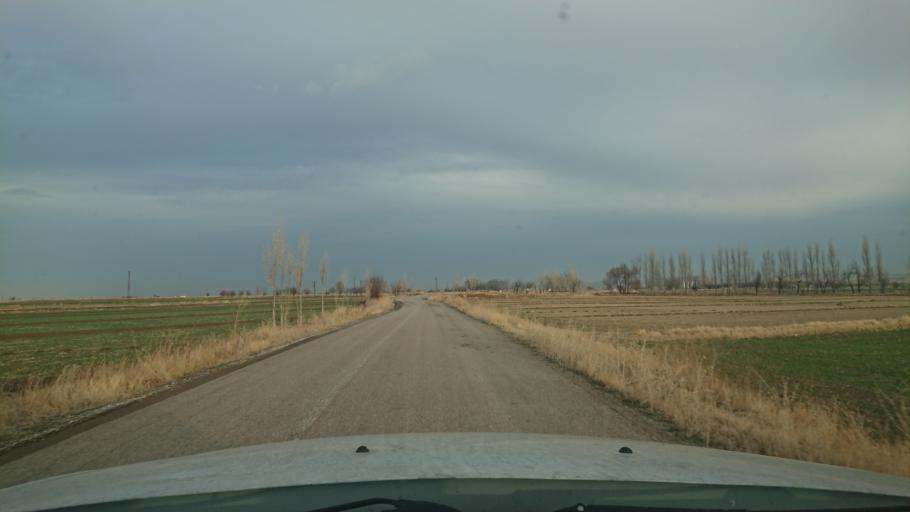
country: TR
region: Aksaray
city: Yesilova
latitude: 38.4406
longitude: 33.8372
